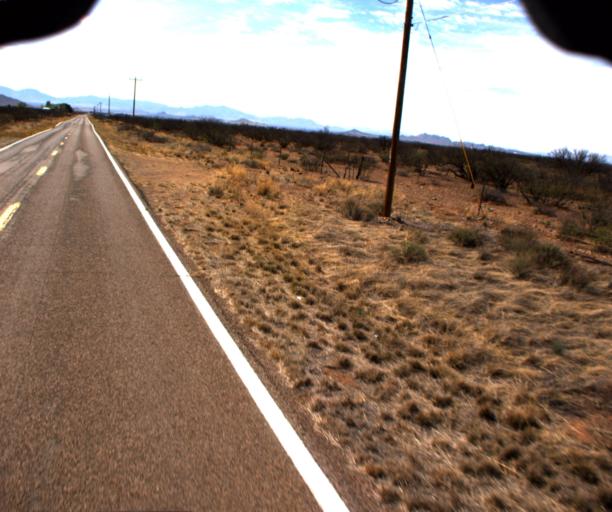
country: US
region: Arizona
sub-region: Cochise County
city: Willcox
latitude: 31.8760
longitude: -109.5675
